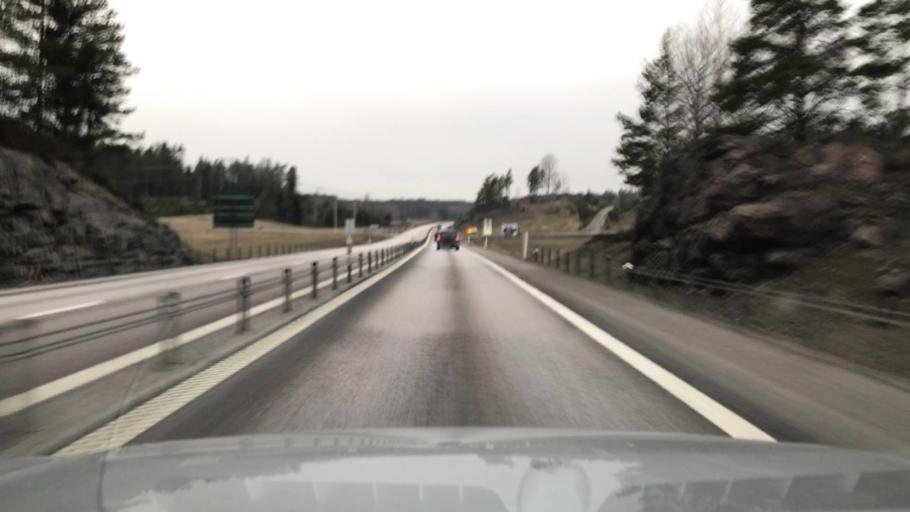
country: SE
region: OEstergoetland
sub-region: Valdemarsviks Kommun
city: Valdemarsvik
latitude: 58.2389
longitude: 16.5456
